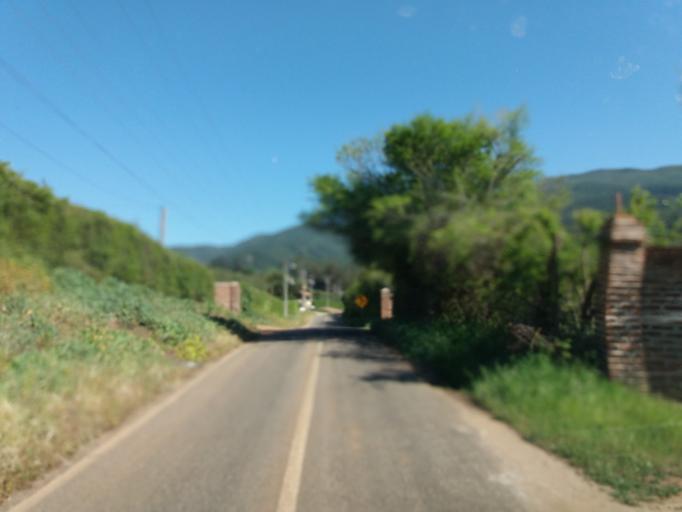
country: CL
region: Valparaiso
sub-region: Provincia de Quillota
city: Quillota
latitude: -32.8560
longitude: -71.2908
